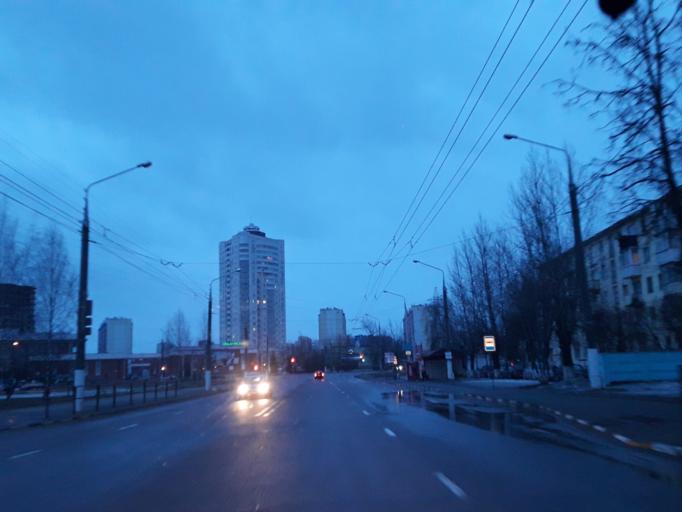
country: BY
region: Vitebsk
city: Vitebsk
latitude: 55.1853
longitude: 30.2281
